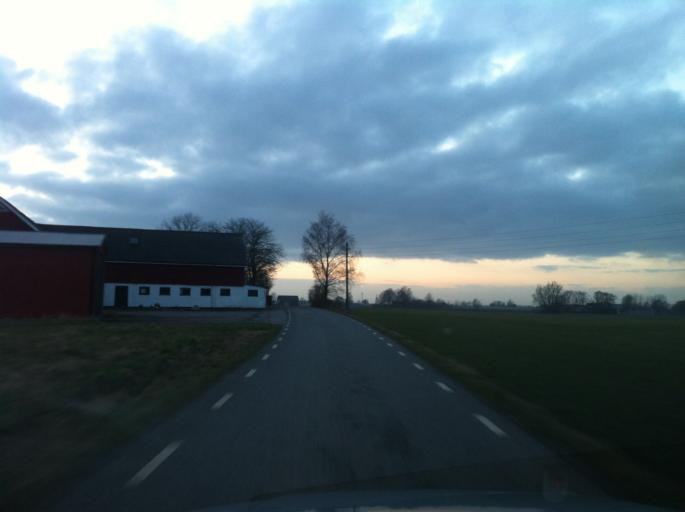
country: SE
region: Skane
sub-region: Svalovs Kommun
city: Teckomatorp
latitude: 55.8566
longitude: 13.0608
